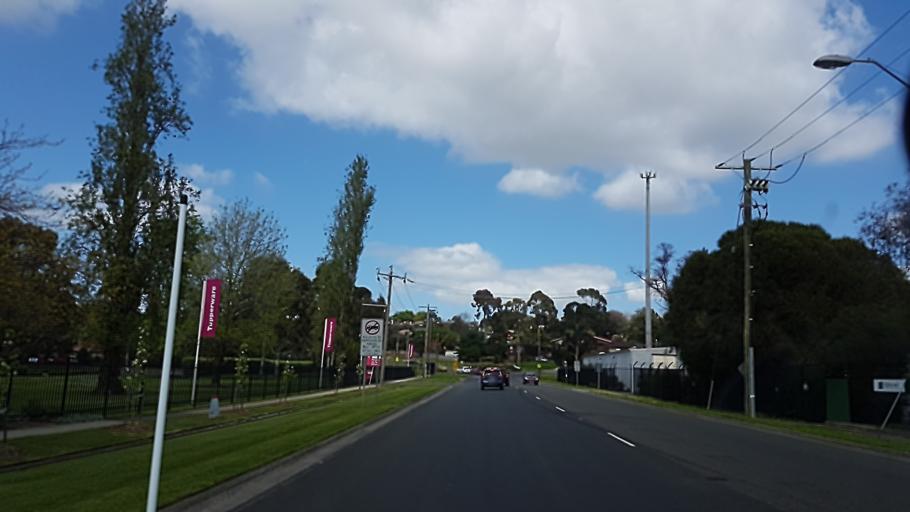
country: AU
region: Victoria
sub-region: Knox
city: Ferntree Gully
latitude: -37.8927
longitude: 145.2935
